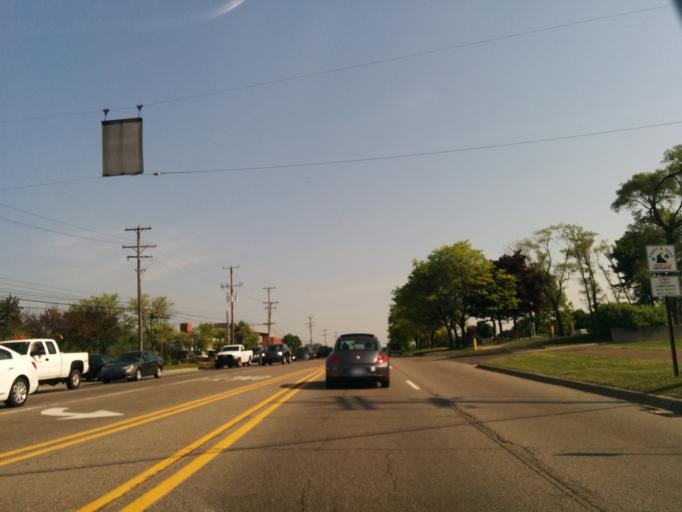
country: US
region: Michigan
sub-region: Oakland County
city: Farmington Hills
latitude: 42.5000
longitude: -83.3586
